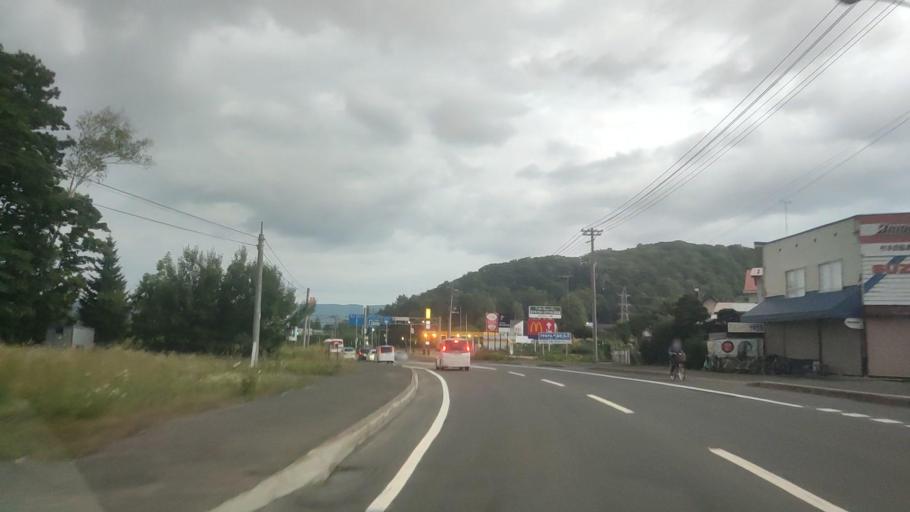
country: JP
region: Hokkaido
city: Shimo-furano
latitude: 43.3459
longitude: 142.3695
